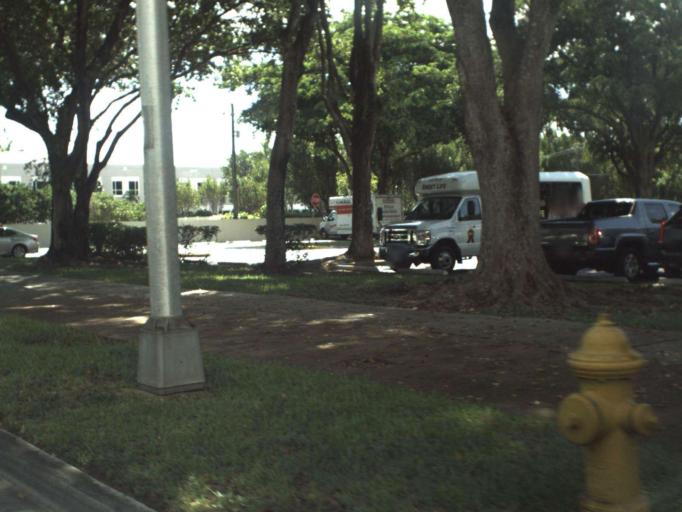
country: US
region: Florida
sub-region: Miami-Dade County
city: Sunset
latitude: 25.7012
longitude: -80.3607
